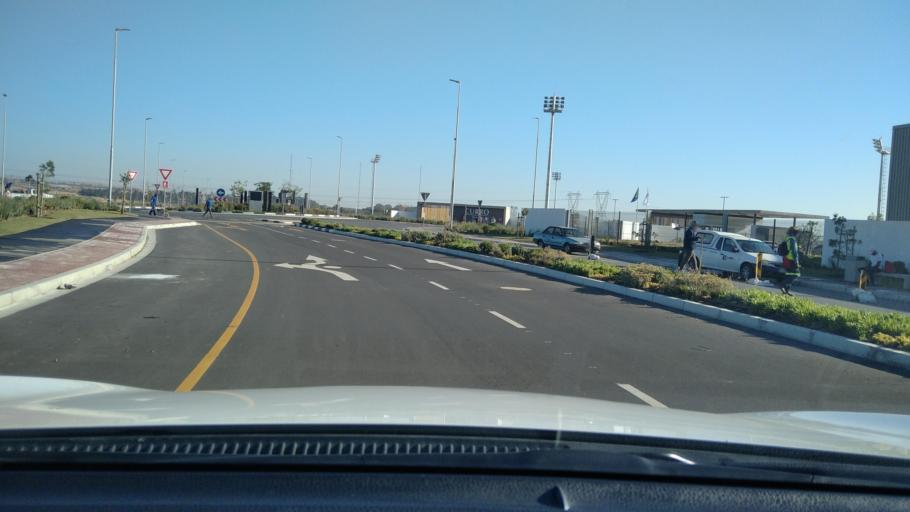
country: ZA
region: Western Cape
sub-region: City of Cape Town
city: Kraaifontein
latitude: -33.8069
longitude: 18.6904
